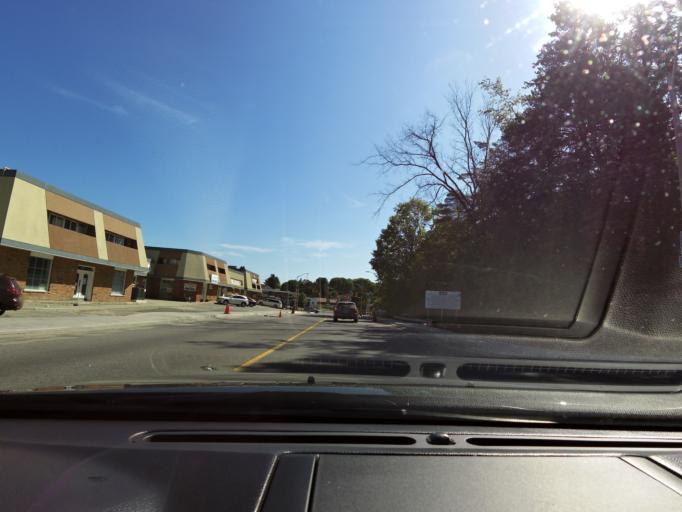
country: CA
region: Ontario
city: Huntsville
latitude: 45.3281
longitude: -79.2132
